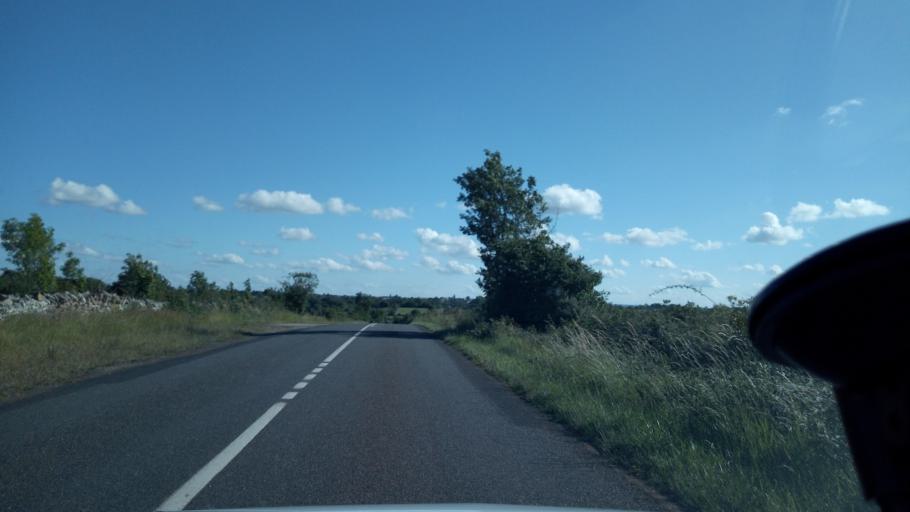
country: FR
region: Midi-Pyrenees
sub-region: Departement de l'Aveyron
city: Sebazac-Concoures
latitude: 44.4218
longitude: 2.6094
